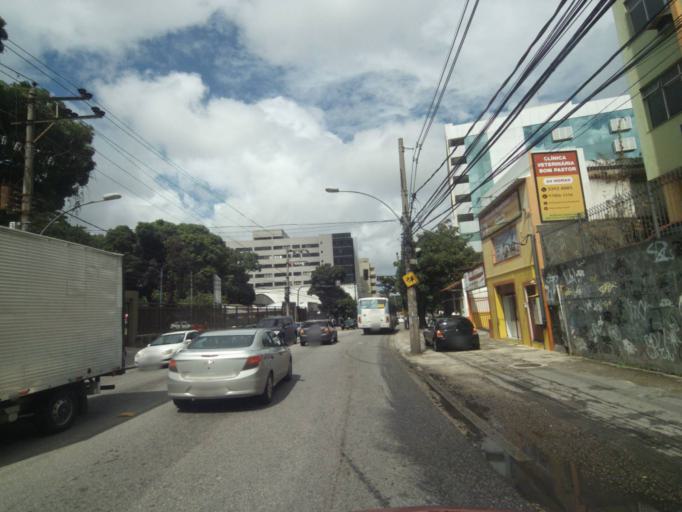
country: BR
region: Rio de Janeiro
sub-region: Sao Joao De Meriti
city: Sao Joao de Meriti
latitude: -22.9300
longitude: -43.3536
